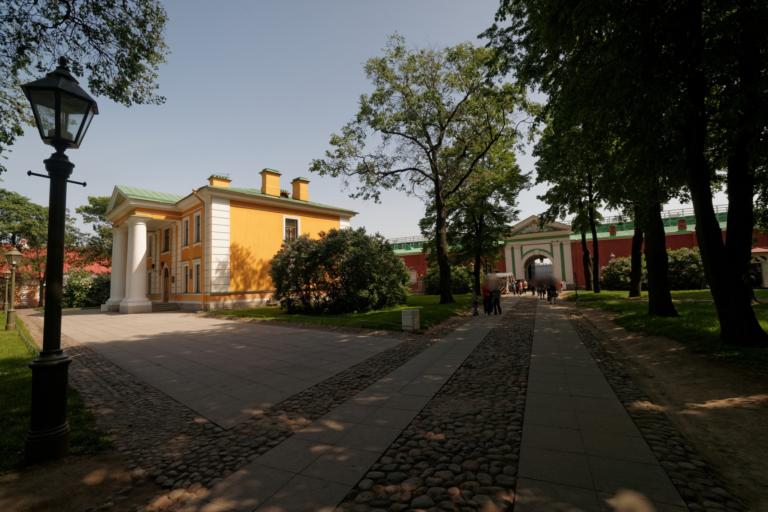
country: RU
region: St.-Petersburg
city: Saint Petersburg
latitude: 59.9497
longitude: 30.3176
